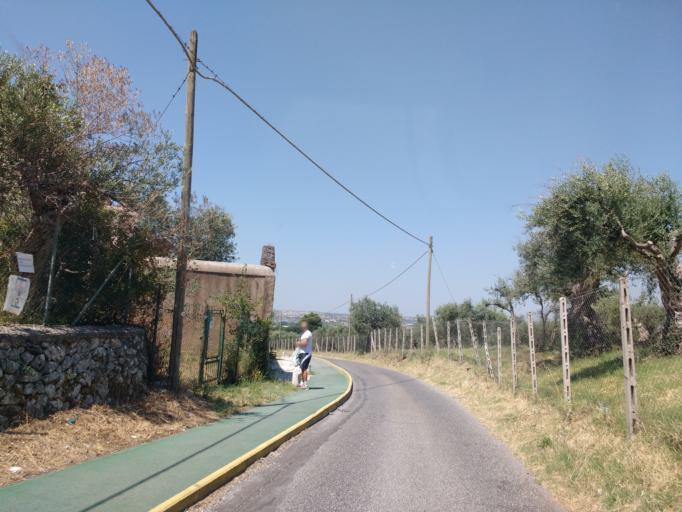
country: IT
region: Latium
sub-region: Citta metropolitana di Roma Capitale
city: Villa Adriana
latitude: 41.9476
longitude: 12.7854
